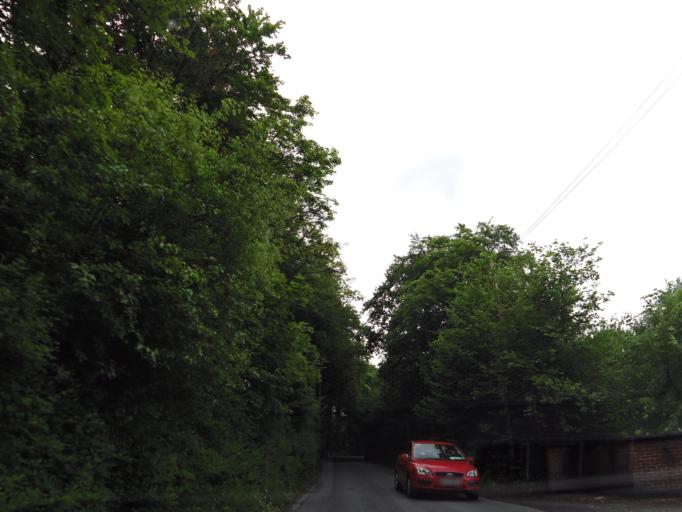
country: IE
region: Munster
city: Thurles
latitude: 52.6622
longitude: -7.7952
